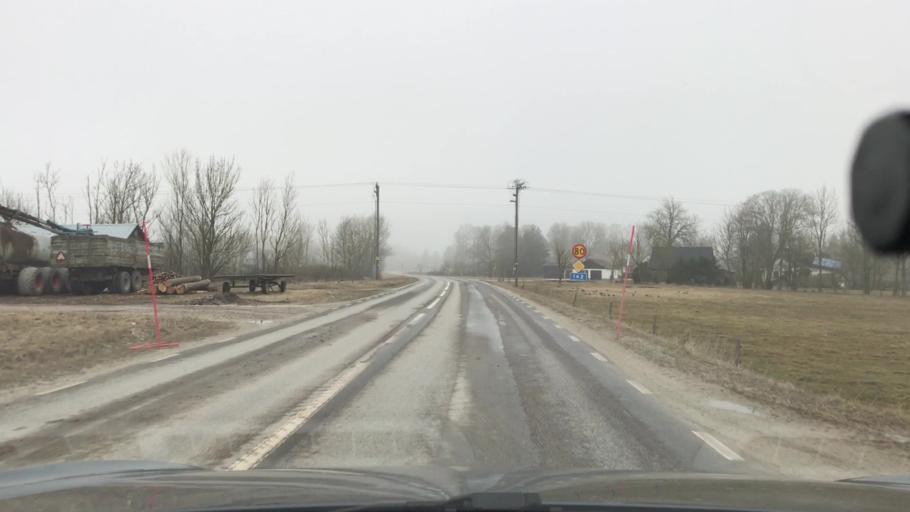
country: SE
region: Gotland
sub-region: Gotland
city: Hemse
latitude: 57.3219
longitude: 18.3846
